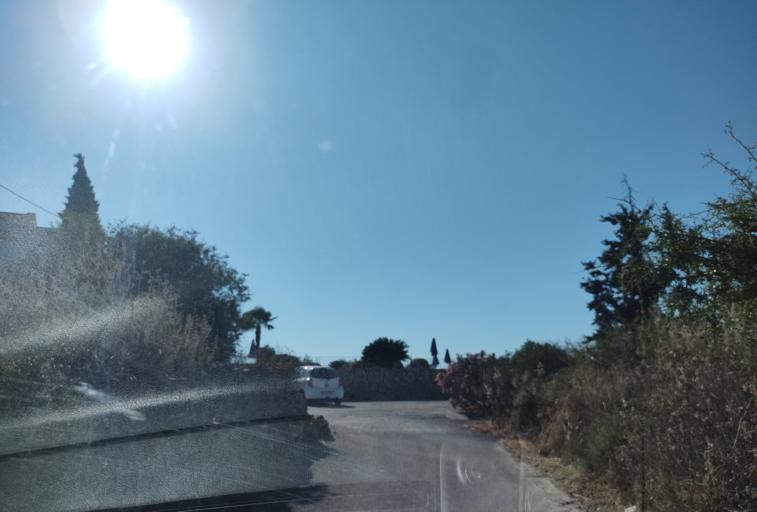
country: GR
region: Crete
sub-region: Nomos Chanias
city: Georgioupolis
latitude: 35.3971
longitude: 24.2344
